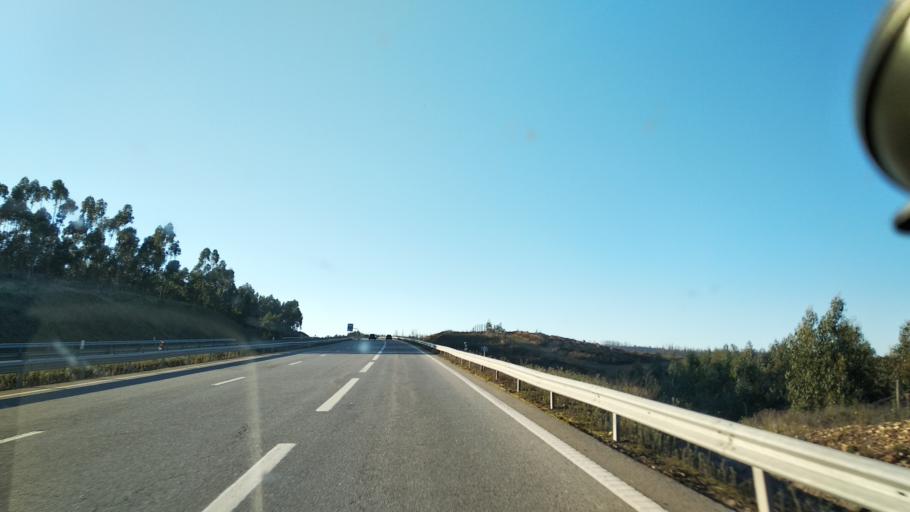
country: PT
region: Portalegre
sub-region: Gaviao
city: Gaviao
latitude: 39.5352
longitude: -7.9159
